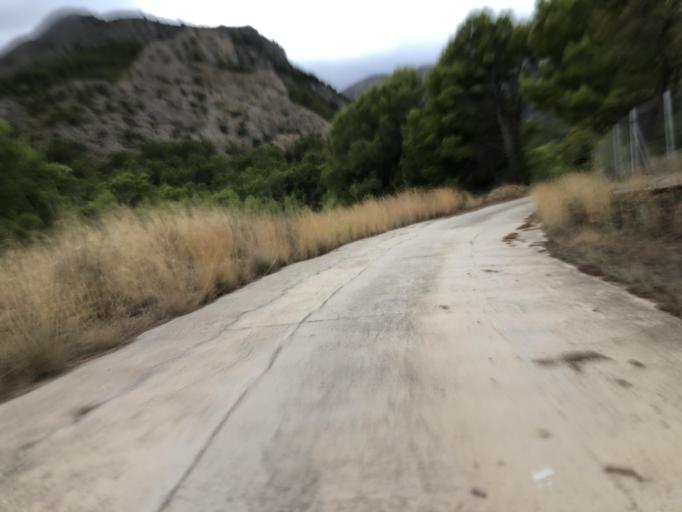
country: ES
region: Valencia
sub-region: Provincia de Alicante
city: Polop
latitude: 38.6365
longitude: -0.1525
